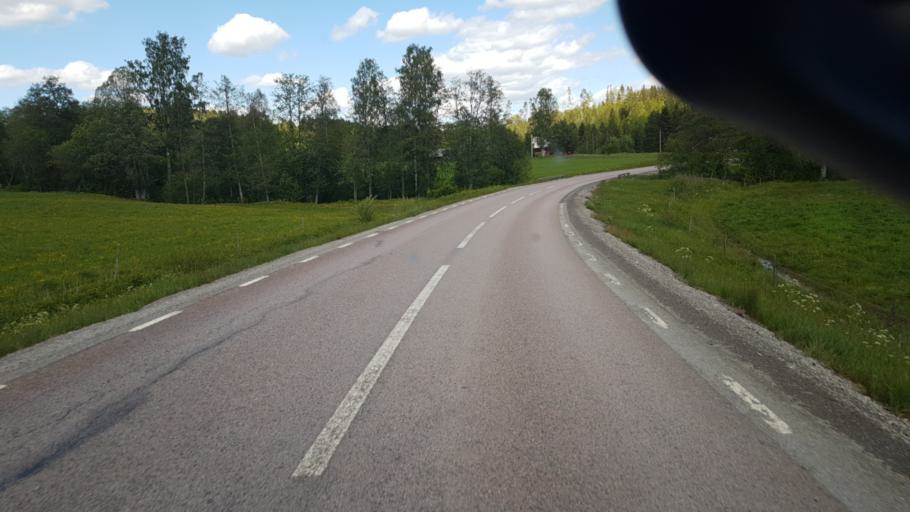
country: SE
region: Vaermland
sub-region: Sunne Kommun
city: Sunne
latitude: 59.6670
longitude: 13.0087
